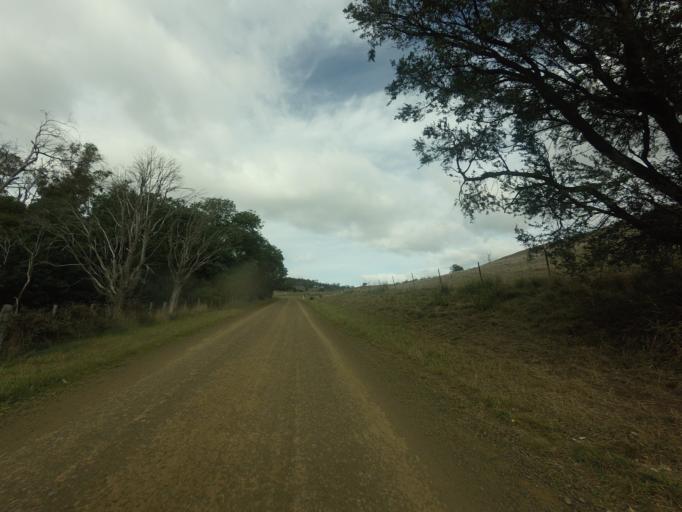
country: AU
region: Tasmania
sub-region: Brighton
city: Bridgewater
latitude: -42.4718
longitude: 147.2873
